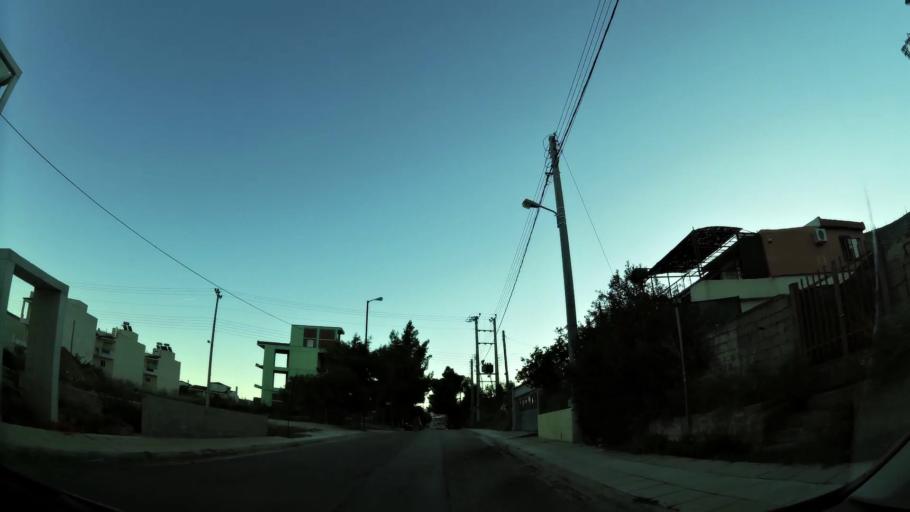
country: GR
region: Attica
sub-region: Nomarchia Anatolikis Attikis
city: Paiania
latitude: 37.9617
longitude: 23.8507
